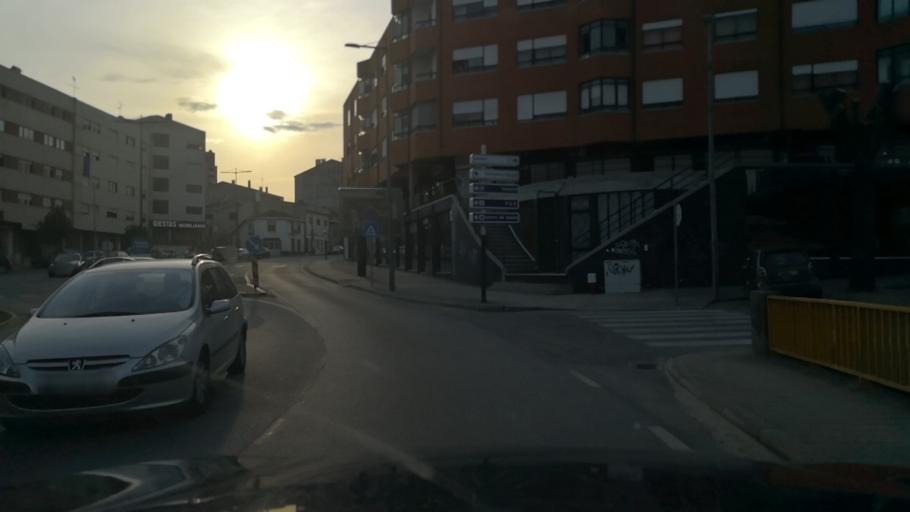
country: PT
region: Porto
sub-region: Valongo
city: Valongo
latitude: 41.1878
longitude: -8.4903
